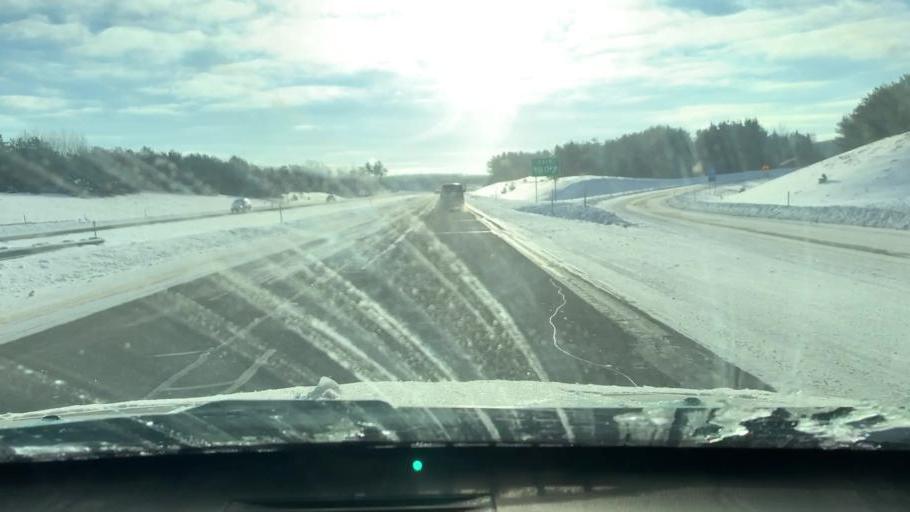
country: US
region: Michigan
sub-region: Wexford County
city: Cadillac
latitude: 44.2573
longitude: -85.3785
